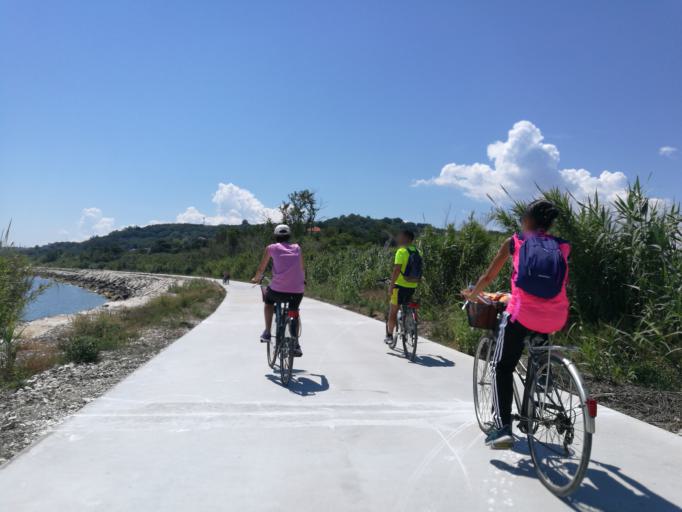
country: IT
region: Abruzzo
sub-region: Provincia di Chieti
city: Marina di San Vito
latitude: 42.3273
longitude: 14.4251
